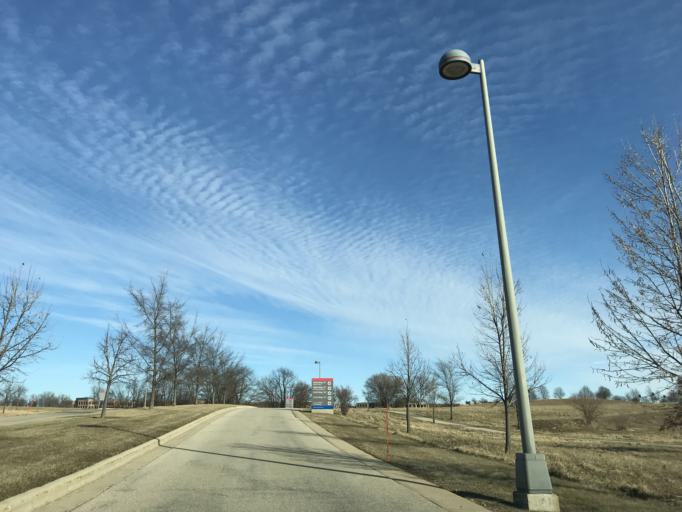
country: US
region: Wisconsin
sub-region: Dane County
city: Windsor
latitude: 43.1542
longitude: -89.2973
